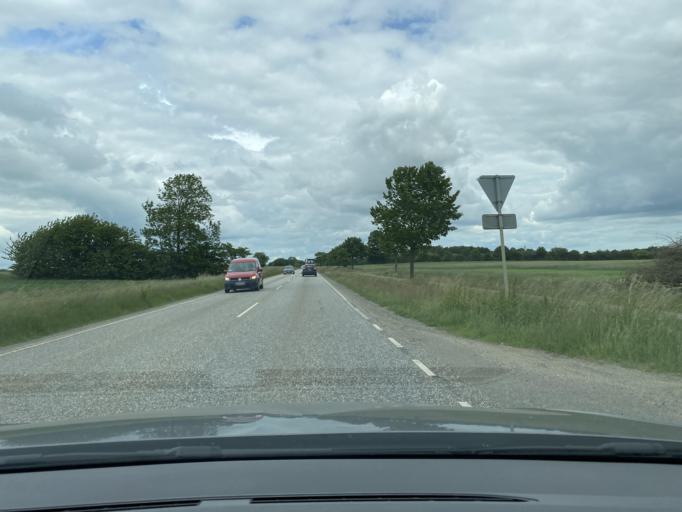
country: DK
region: South Denmark
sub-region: Vejle Kommune
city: Jelling
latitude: 55.6656
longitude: 9.4134
